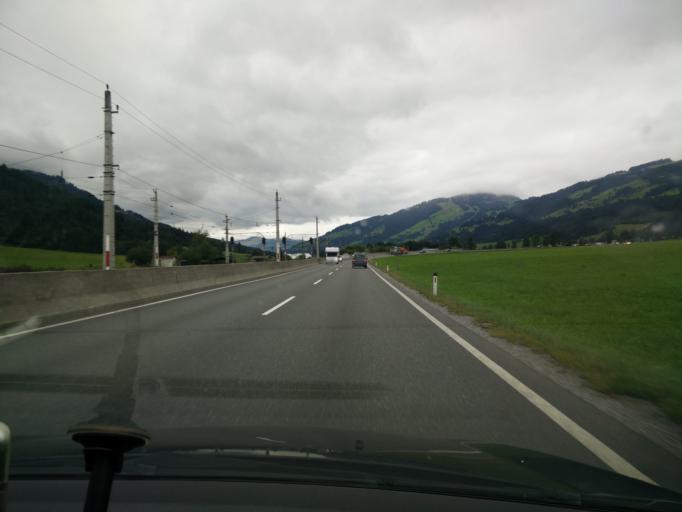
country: AT
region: Tyrol
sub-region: Politischer Bezirk Kitzbuhel
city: Kirchberg in Tirol
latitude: 47.4493
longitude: 12.3049
